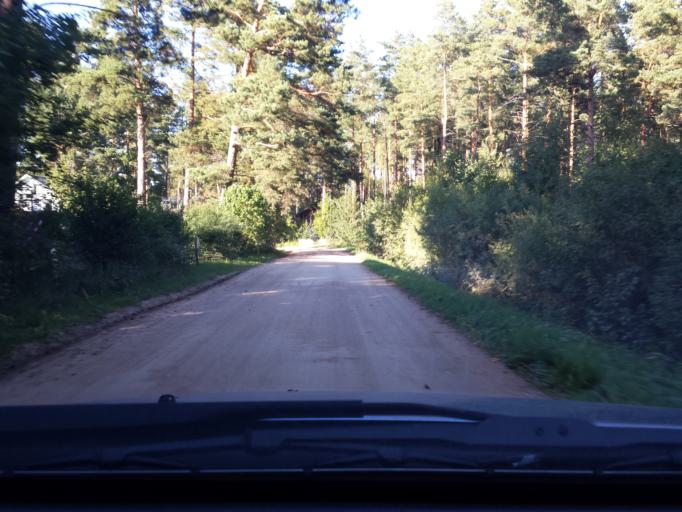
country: LV
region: Carnikava
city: Carnikava
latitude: 57.1210
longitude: 24.2400
